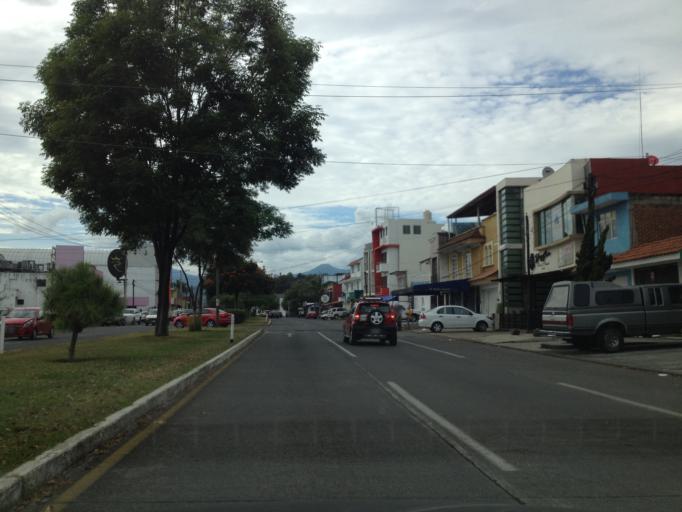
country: MX
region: Michoacan
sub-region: Uruapan
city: Uruapan
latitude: 19.4045
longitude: -102.0475
